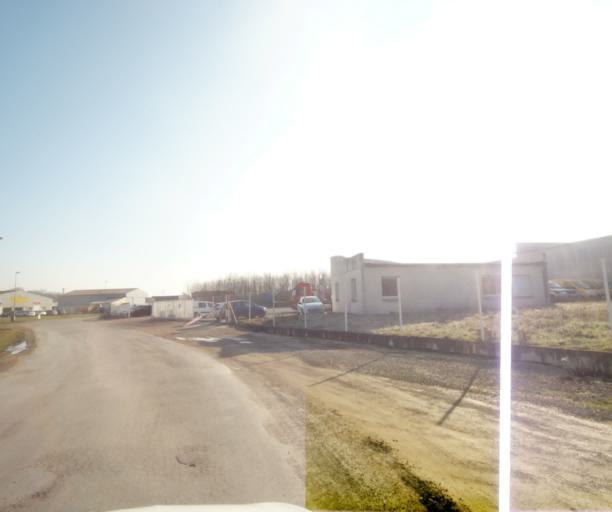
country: FR
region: Champagne-Ardenne
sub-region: Departement de la Haute-Marne
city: Wassy
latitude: 48.5001
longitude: 4.9350
